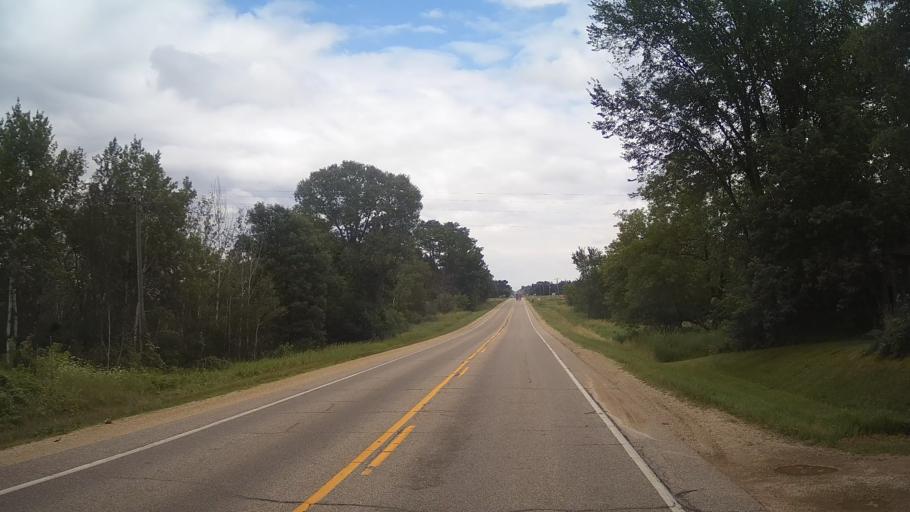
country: US
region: Wisconsin
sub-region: Waushara County
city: Wautoma
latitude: 44.0684
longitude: -89.3605
